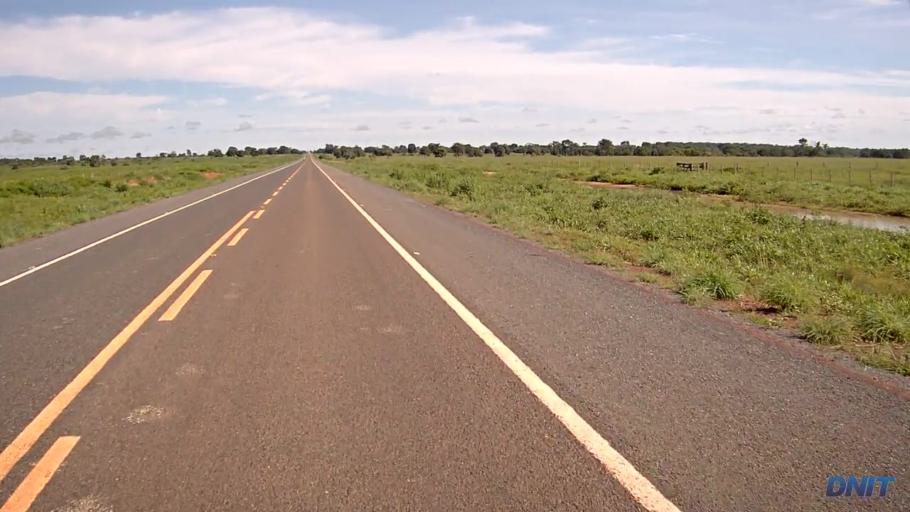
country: BR
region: Goias
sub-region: Sao Miguel Do Araguaia
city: Sao Miguel do Araguaia
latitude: -13.4817
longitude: -50.1117
